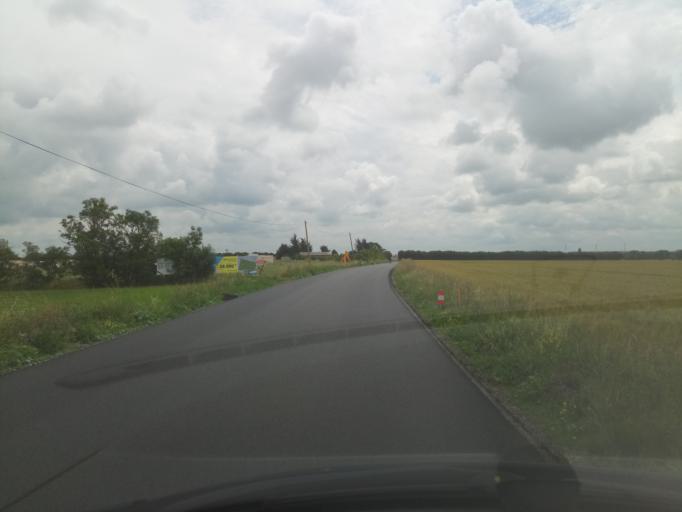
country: FR
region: Poitou-Charentes
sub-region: Departement de la Charente-Maritime
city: Saint-Jean-de-Liversay
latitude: 46.2699
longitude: -0.8888
